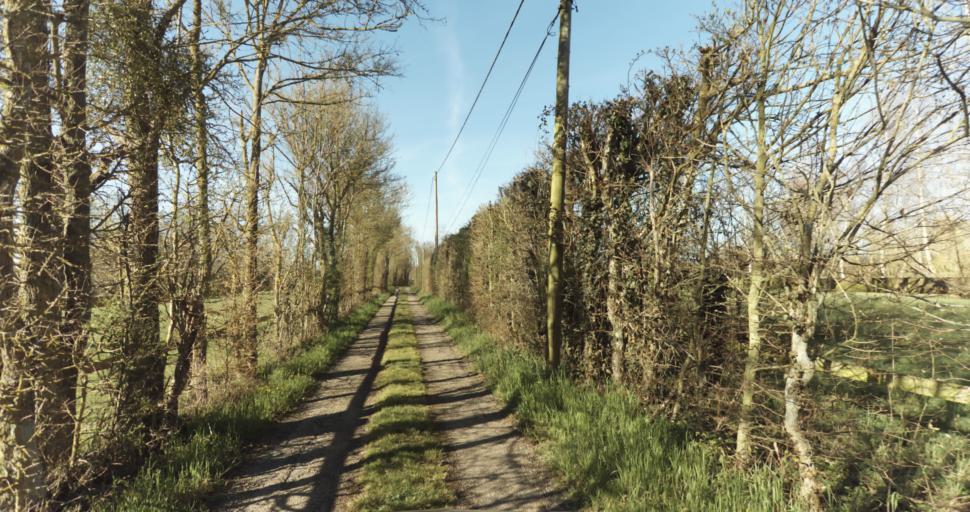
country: FR
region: Lower Normandy
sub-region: Departement du Calvados
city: Saint-Pierre-sur-Dives
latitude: 49.0466
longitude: 0.0592
